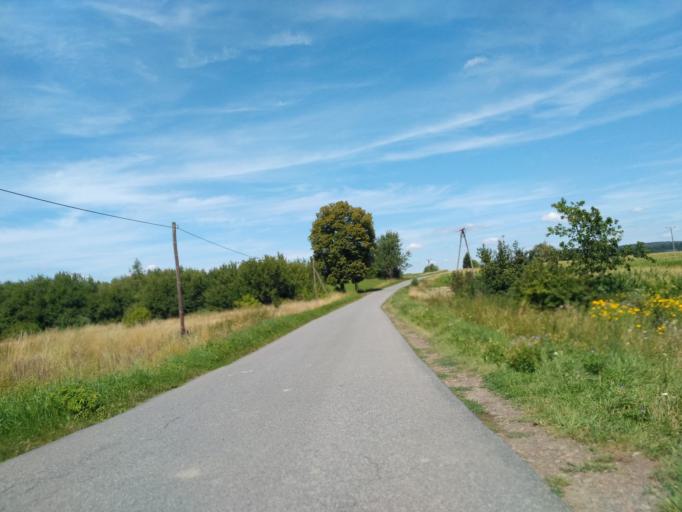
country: PL
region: Subcarpathian Voivodeship
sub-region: Powiat sanocki
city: Strachocina
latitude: 49.5808
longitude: 22.1242
